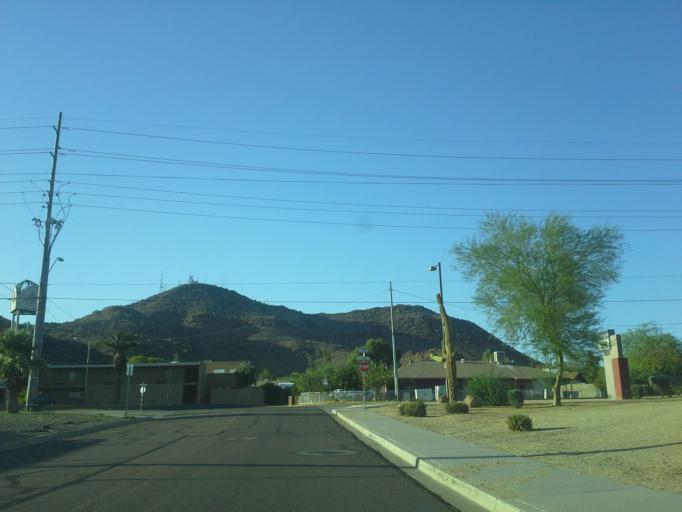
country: US
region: Arizona
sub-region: Maricopa County
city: Glendale
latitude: 33.5817
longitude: -112.0847
